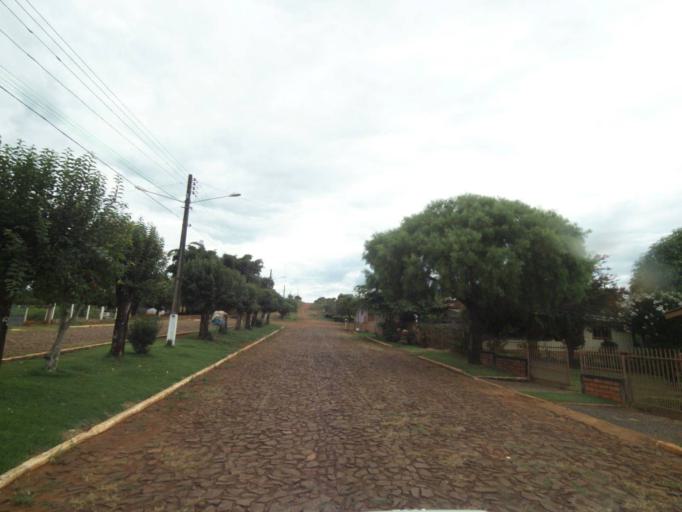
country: BR
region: Parana
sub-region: Guaraniacu
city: Guaraniacu
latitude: -24.9205
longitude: -52.9385
